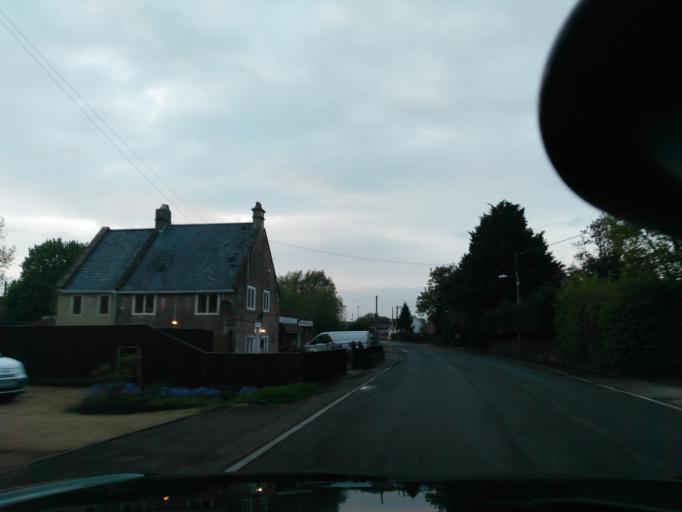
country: GB
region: England
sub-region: Wiltshire
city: Melksham
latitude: 51.3592
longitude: -2.1437
